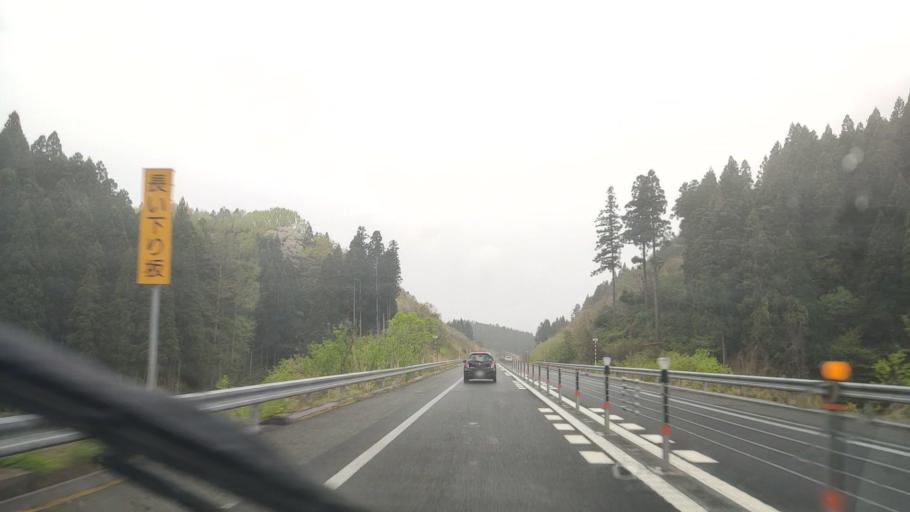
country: JP
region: Akita
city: Noshiromachi
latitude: 40.1964
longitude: 140.1234
